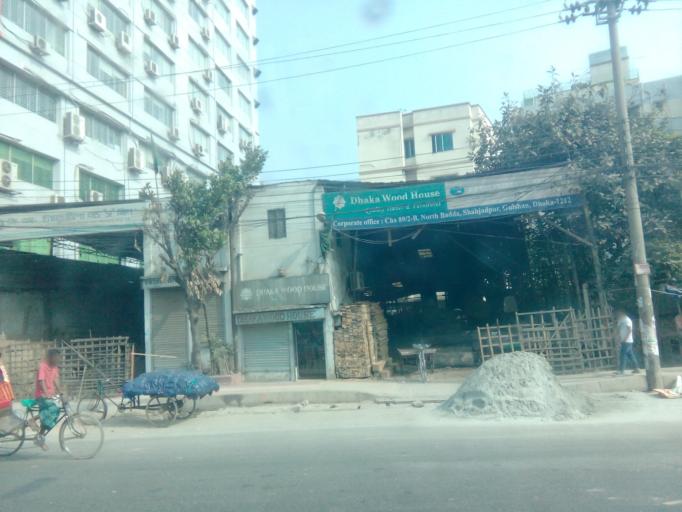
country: BD
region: Dhaka
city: Paltan
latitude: 23.7880
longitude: 90.4254
